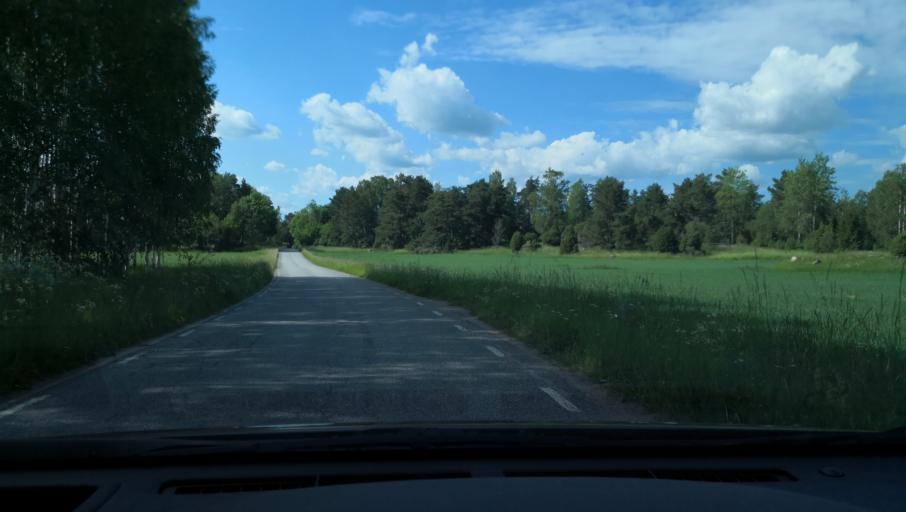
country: SE
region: Uppsala
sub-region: Enkopings Kommun
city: Orsundsbro
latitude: 59.8236
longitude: 17.3228
